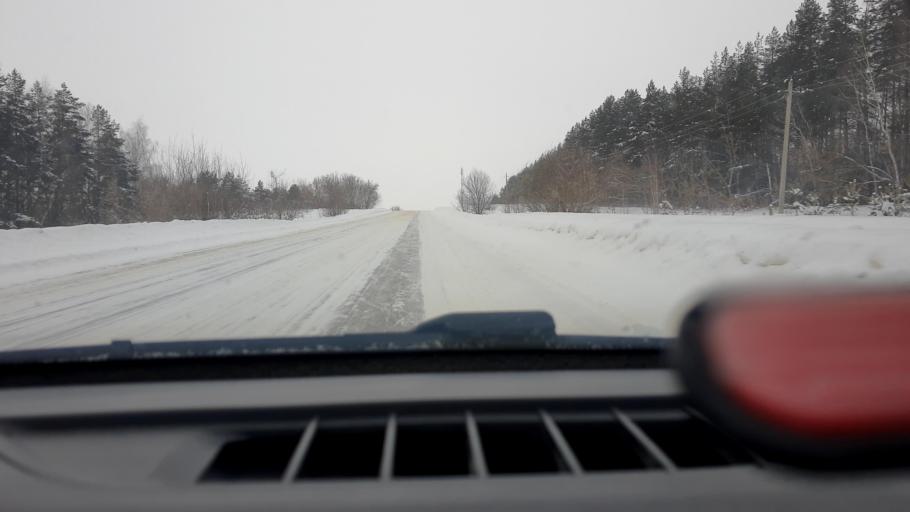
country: RU
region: Nizjnij Novgorod
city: Buturlino
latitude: 55.5967
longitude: 44.8928
